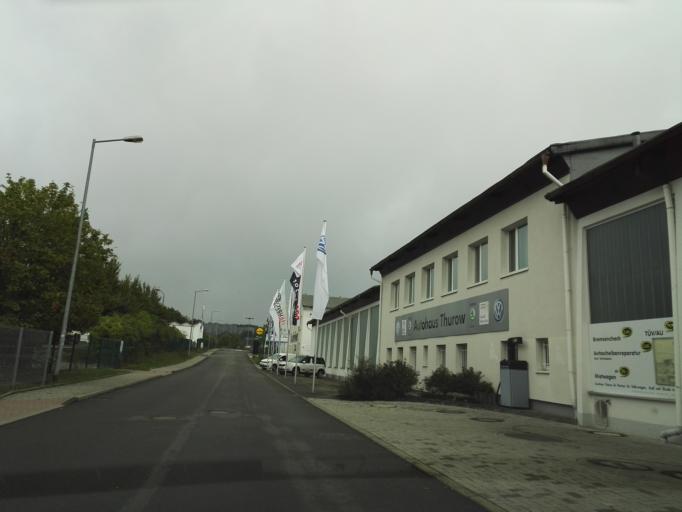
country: DE
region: Thuringia
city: Ilmenau
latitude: 50.6894
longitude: 10.9227
